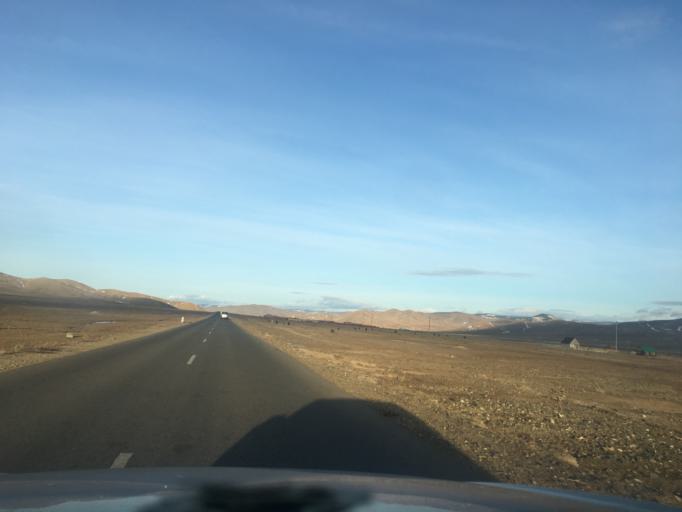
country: MN
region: Central Aimak
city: Mandal
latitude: 48.0958
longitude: 106.6118
